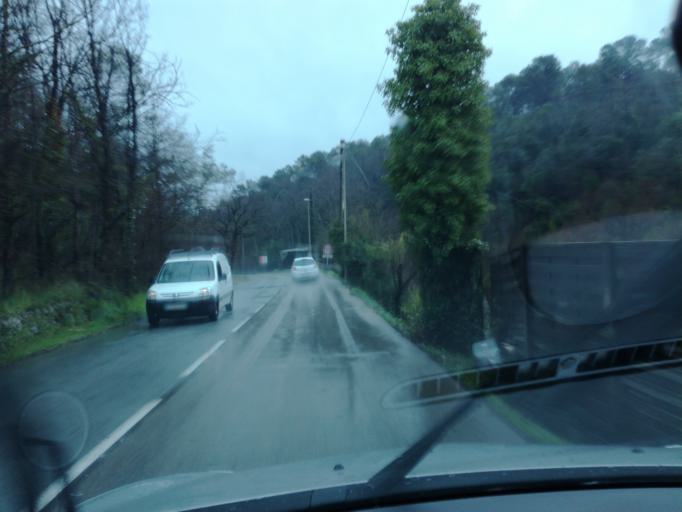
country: FR
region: Provence-Alpes-Cote d'Azur
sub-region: Departement des Alpes-Maritimes
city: Valbonne
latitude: 43.6401
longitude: 6.9917
